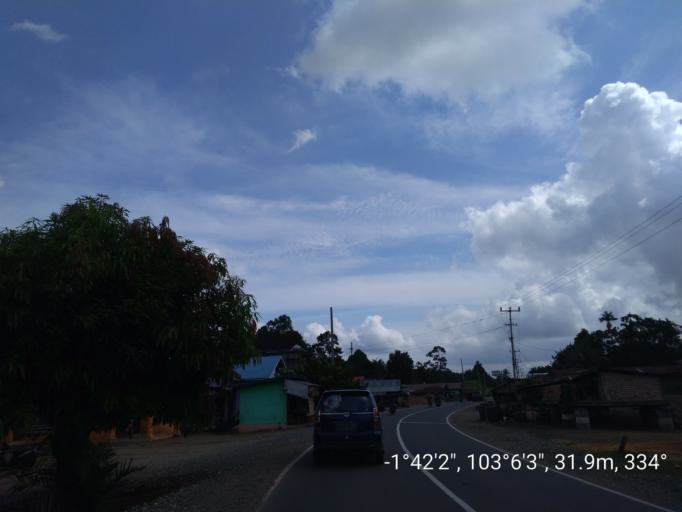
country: ID
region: Jambi
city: Muara Tembesi
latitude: -1.7007
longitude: 103.1013
